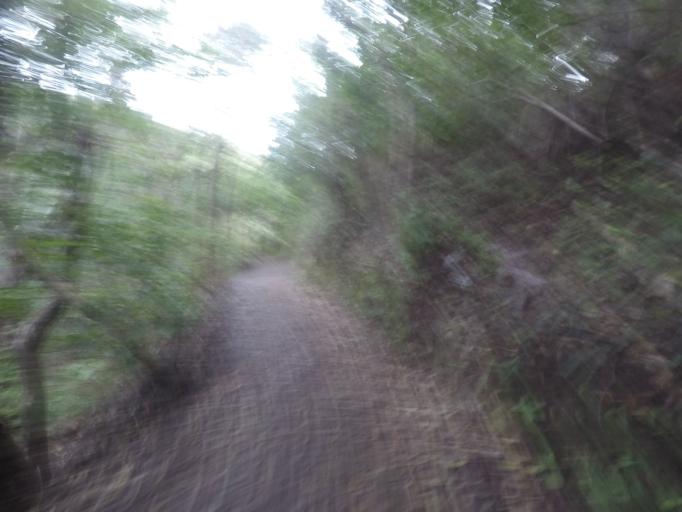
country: NZ
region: Bay of Plenty
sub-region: Western Bay of Plenty District
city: Waihi Beach
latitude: -37.3918
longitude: 175.9409
